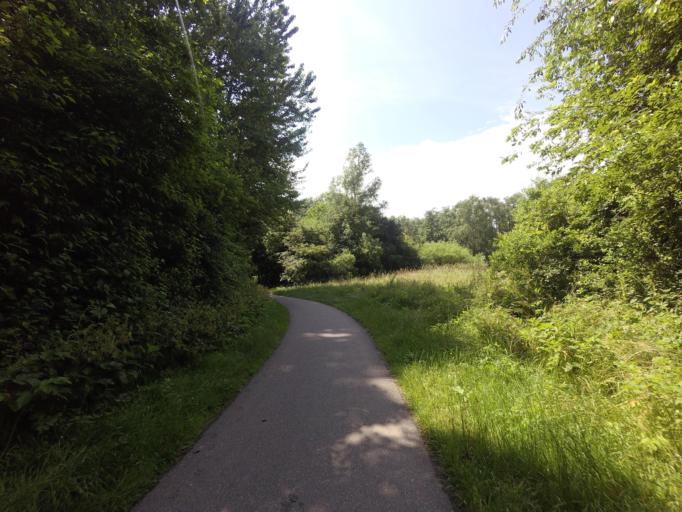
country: NL
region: North Holland
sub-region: Gemeente Enkhuizen
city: Enkhuizen
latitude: 52.7114
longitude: 5.2557
